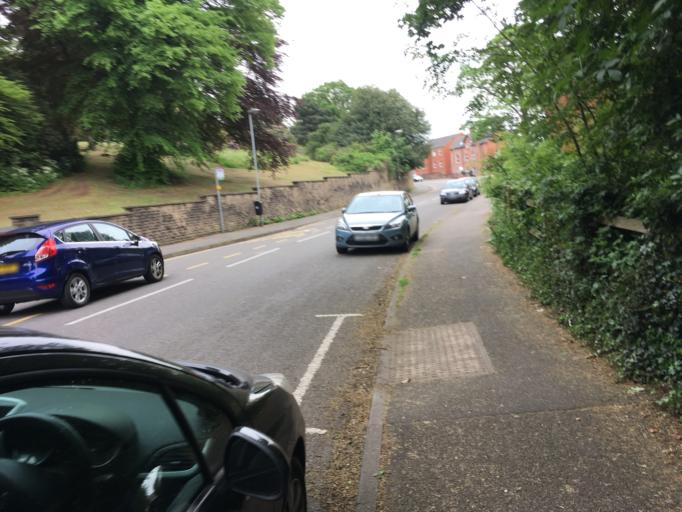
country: GB
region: England
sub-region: Derbyshire
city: Chesterfield
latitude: 53.2326
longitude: -1.4183
